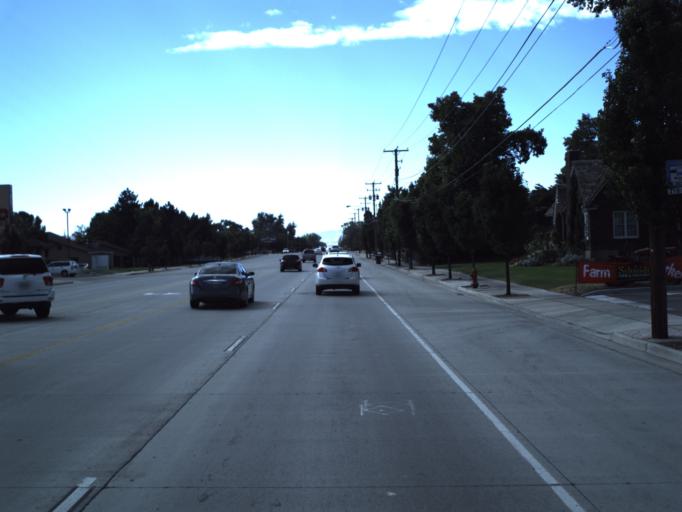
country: US
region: Utah
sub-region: Salt Lake County
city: South Jordan Heights
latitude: 40.5849
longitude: -111.9388
